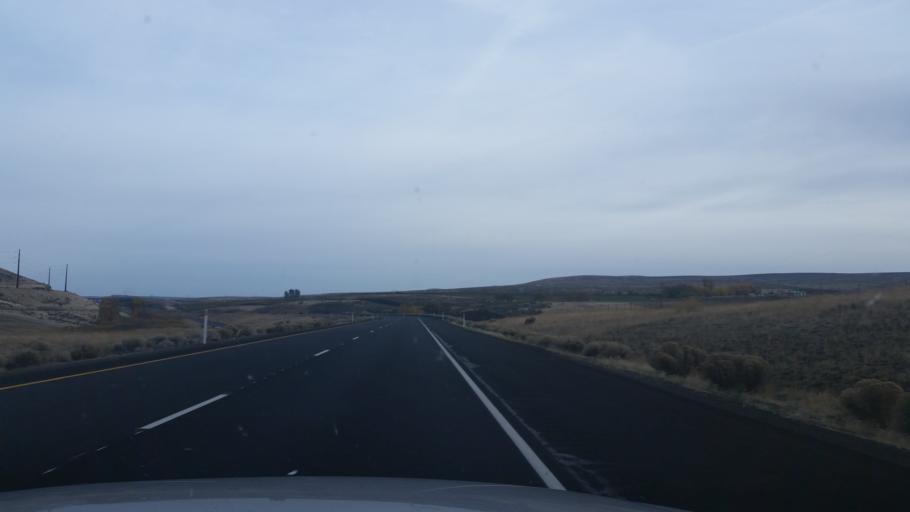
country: US
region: Washington
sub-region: Kittitas County
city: Kittitas
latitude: 46.9628
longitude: -120.3313
